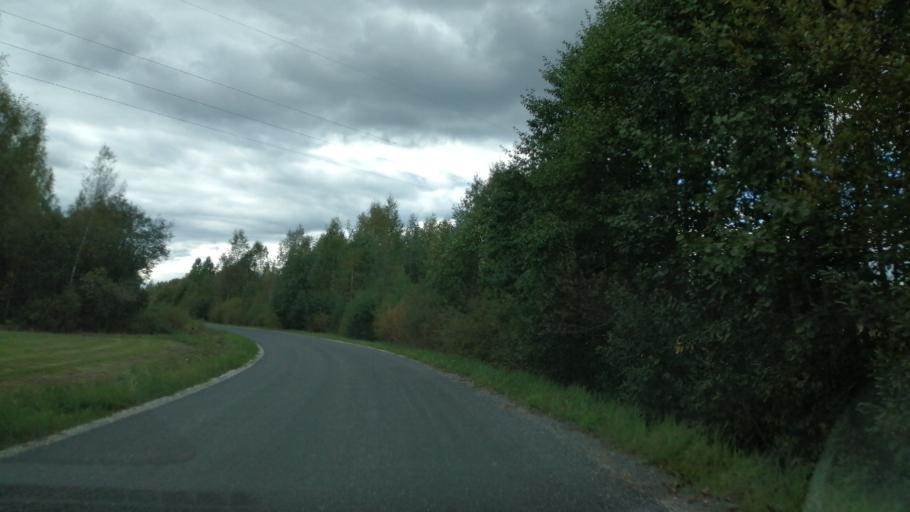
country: EE
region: Jaervamaa
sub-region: Tueri vald
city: Tueri
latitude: 58.8062
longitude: 25.4577
